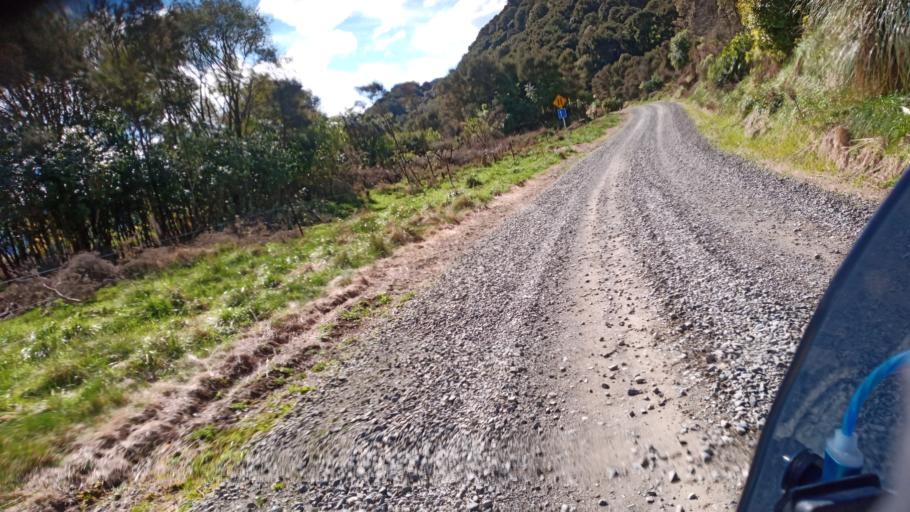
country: NZ
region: Hawke's Bay
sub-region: Wairoa District
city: Wairoa
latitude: -38.8307
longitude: 177.1620
